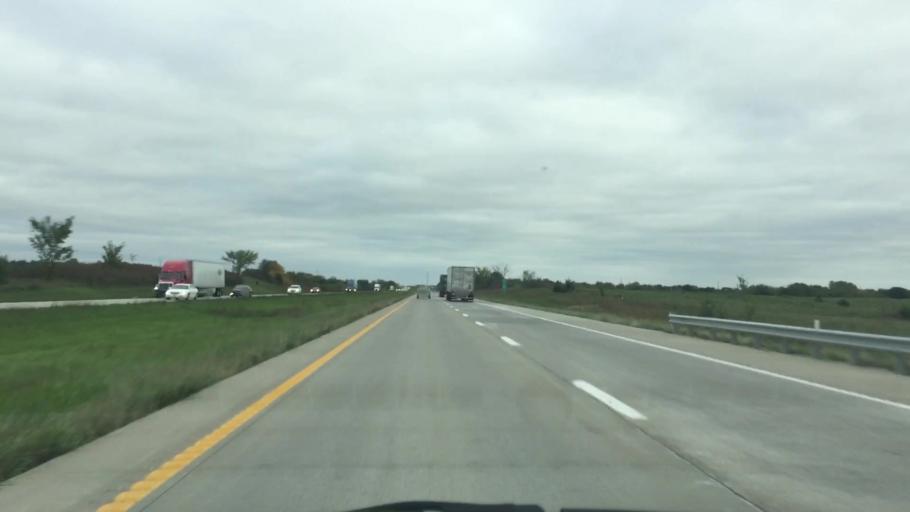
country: US
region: Missouri
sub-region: Clinton County
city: Lathrop
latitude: 39.6155
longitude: -94.2492
